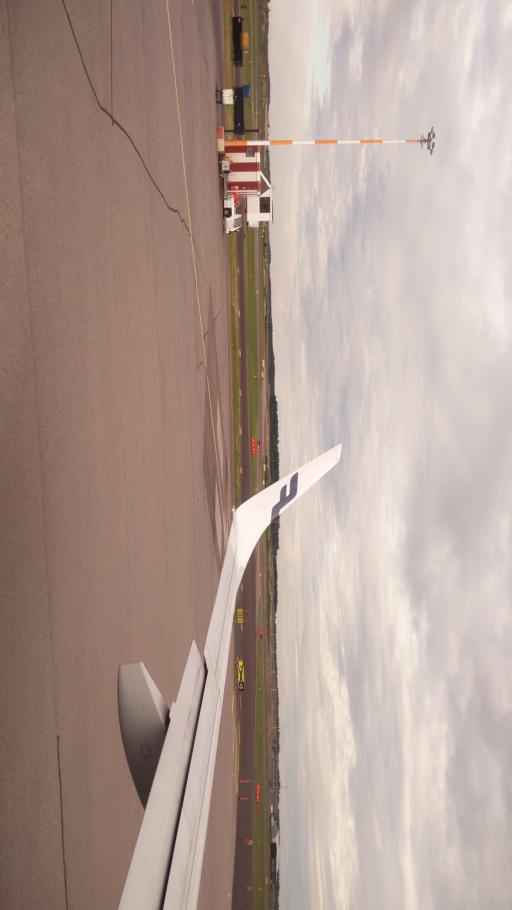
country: FI
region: Uusimaa
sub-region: Helsinki
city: Vantaa
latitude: 60.3180
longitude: 24.9606
